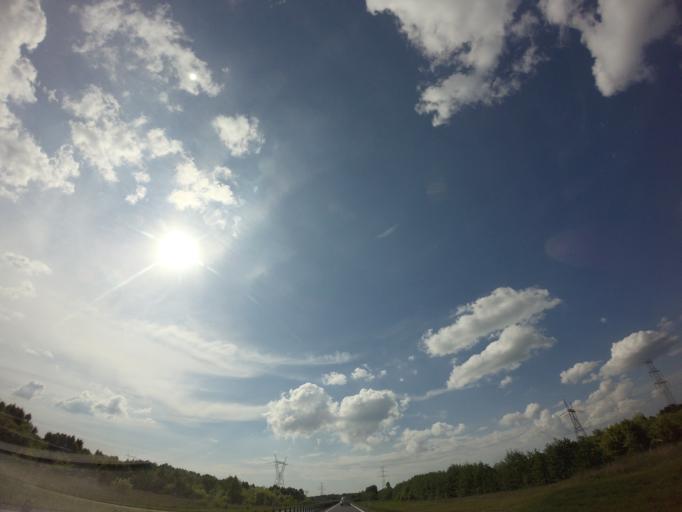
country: PL
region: West Pomeranian Voivodeship
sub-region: Powiat stargardzki
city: Kobylanka
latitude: 53.3611
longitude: 14.9078
